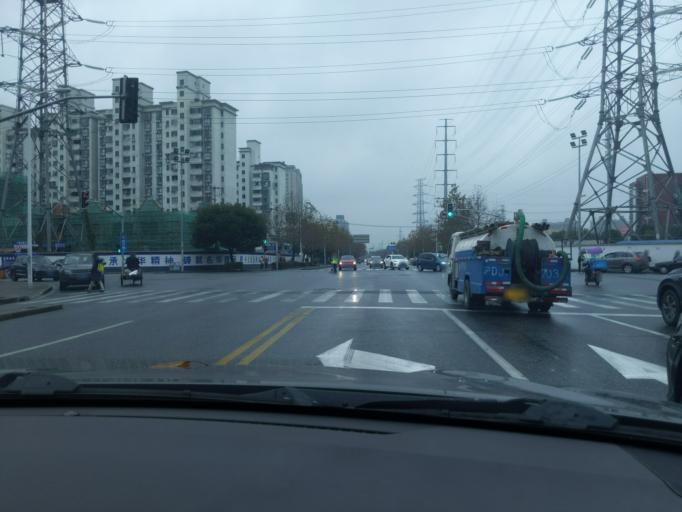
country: CN
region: Shanghai Shi
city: Huamu
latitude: 31.1872
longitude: 121.5258
